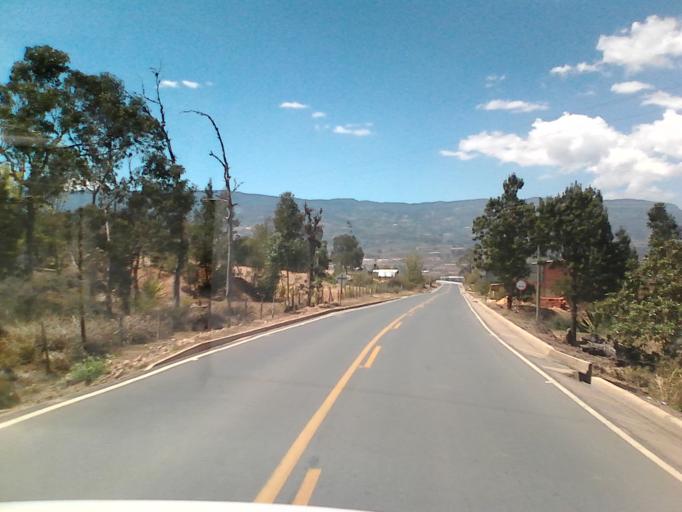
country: CO
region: Boyaca
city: Villa de Leiva
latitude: 5.6234
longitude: -73.5826
